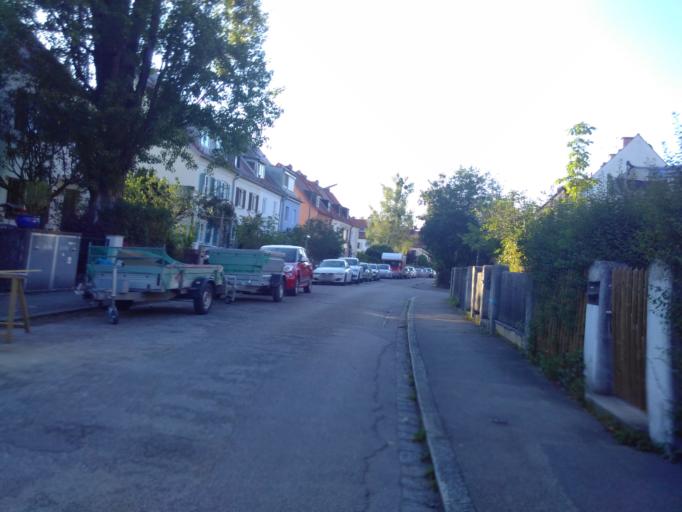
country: DE
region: Bavaria
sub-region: Upper Bavaria
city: Pasing
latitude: 48.1306
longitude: 11.4840
